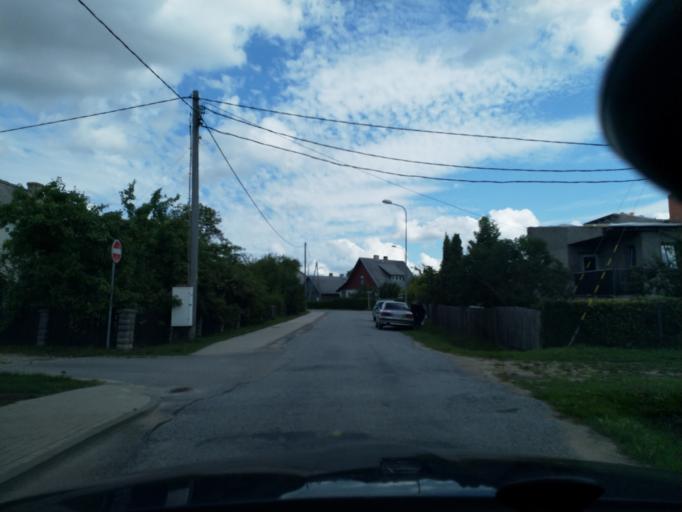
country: LV
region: Kuldigas Rajons
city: Kuldiga
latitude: 56.9637
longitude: 21.9926
